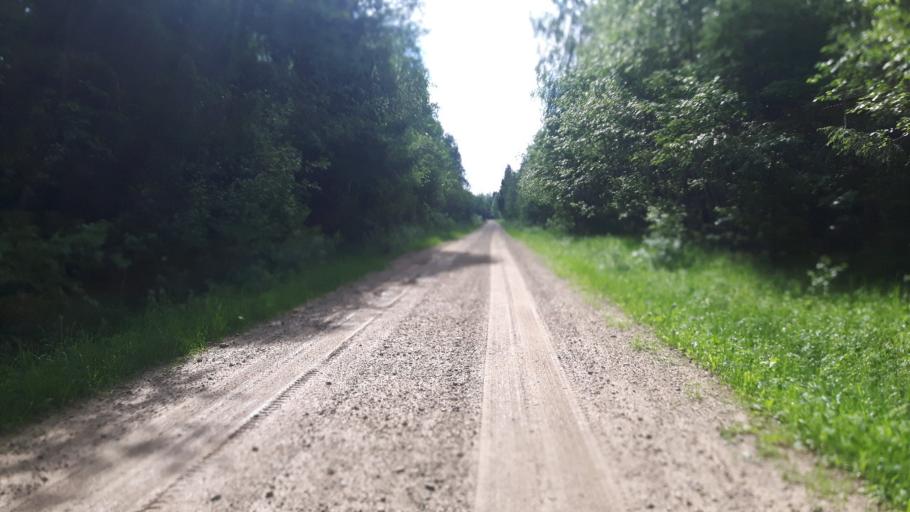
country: EE
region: Paernumaa
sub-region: Vaendra vald (alev)
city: Vandra
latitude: 58.7328
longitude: 25.0048
